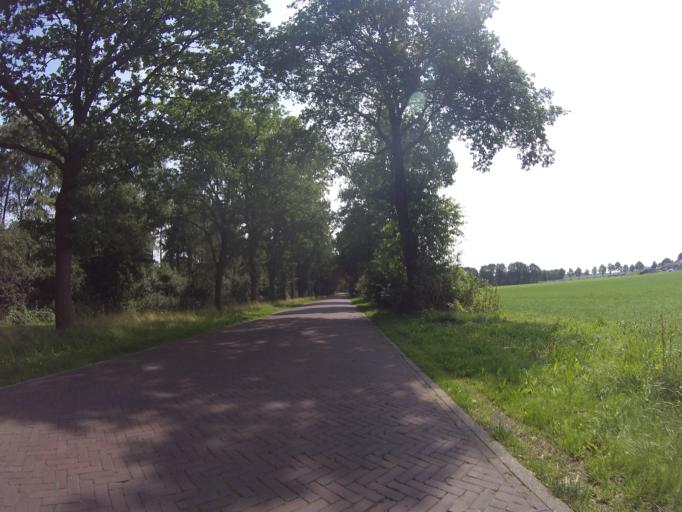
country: NL
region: Drenthe
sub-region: Gemeente Coevorden
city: Sleen
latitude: 52.7951
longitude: 6.7010
